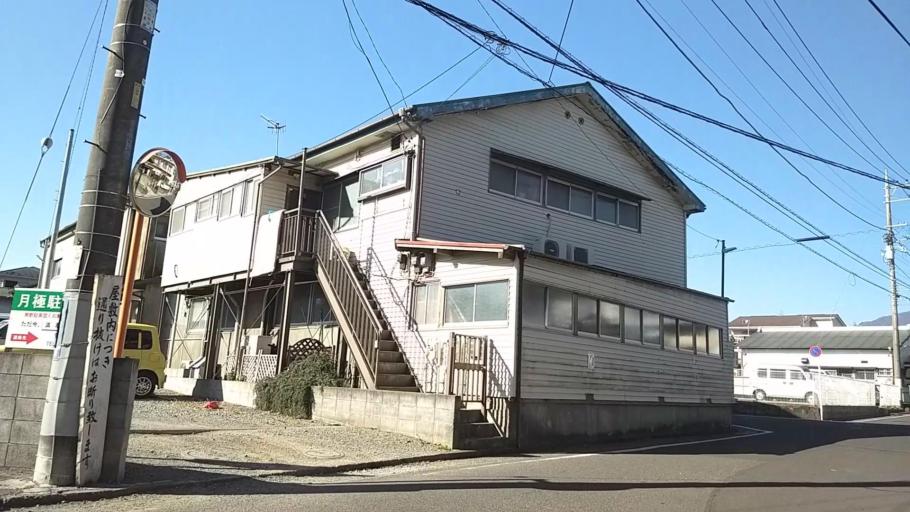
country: JP
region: Kanagawa
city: Hadano
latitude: 35.3778
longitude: 139.2257
